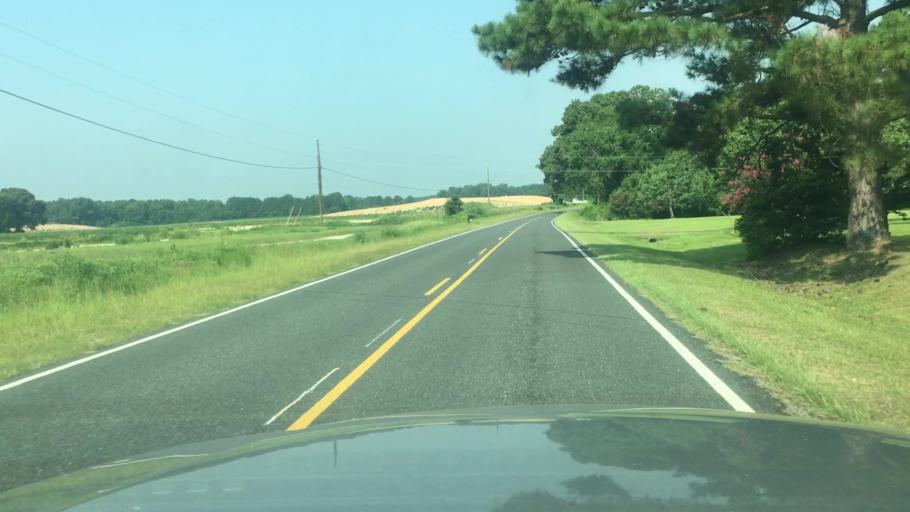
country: US
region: North Carolina
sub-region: Cumberland County
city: Hope Mills
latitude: 34.9093
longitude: -78.8603
